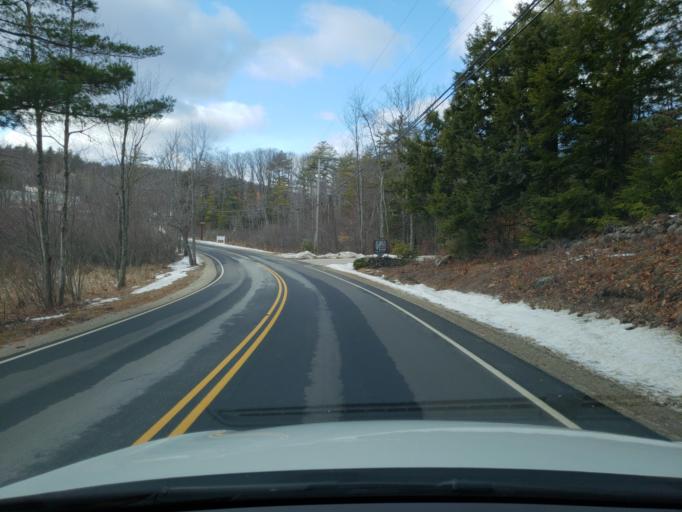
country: US
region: New Hampshire
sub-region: Hillsborough County
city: Greenfield
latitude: 43.0130
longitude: -71.8752
